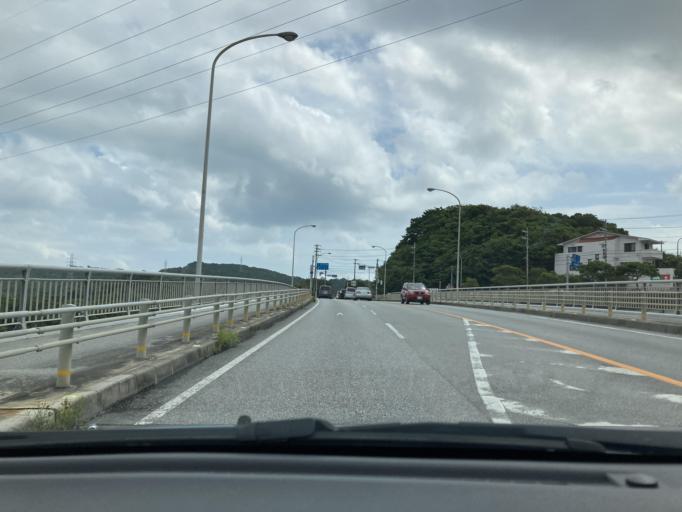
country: JP
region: Okinawa
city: Chatan
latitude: 26.2900
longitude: 127.7852
